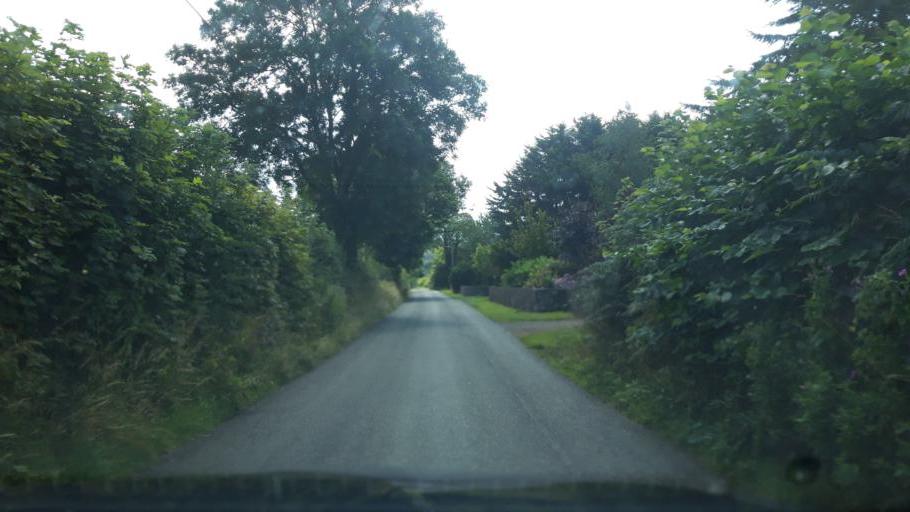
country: IE
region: Leinster
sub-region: Kilkenny
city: Graiguenamanagh
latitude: 52.5475
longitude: -6.9679
